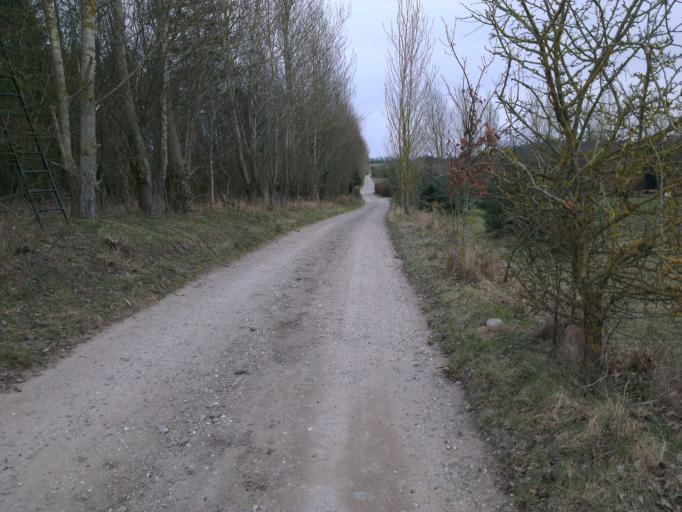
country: DK
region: Capital Region
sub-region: Frederikssund Kommune
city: Jaegerspris
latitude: 55.8387
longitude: 12.0155
